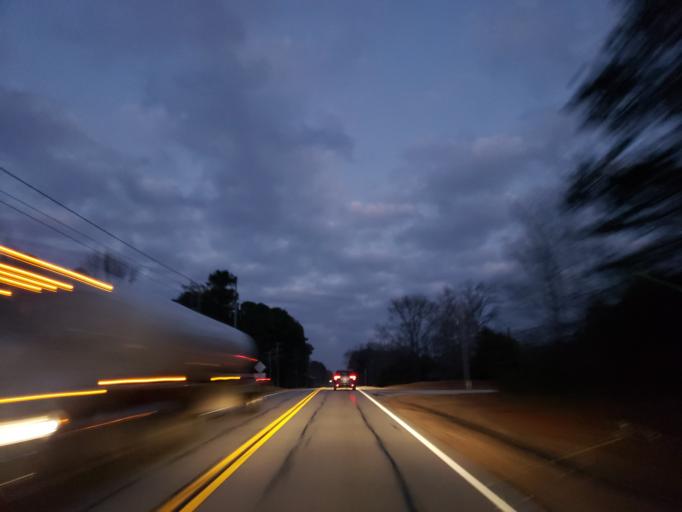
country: US
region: Georgia
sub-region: Carroll County
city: Temple
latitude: 33.8387
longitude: -84.9992
